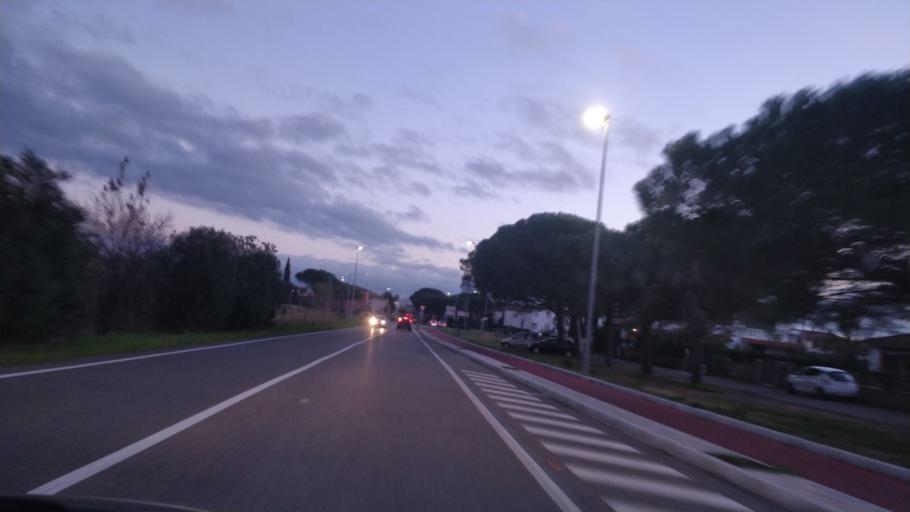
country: IT
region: Tuscany
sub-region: Provincia di Livorno
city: Vada
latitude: 43.3566
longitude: 10.4549
